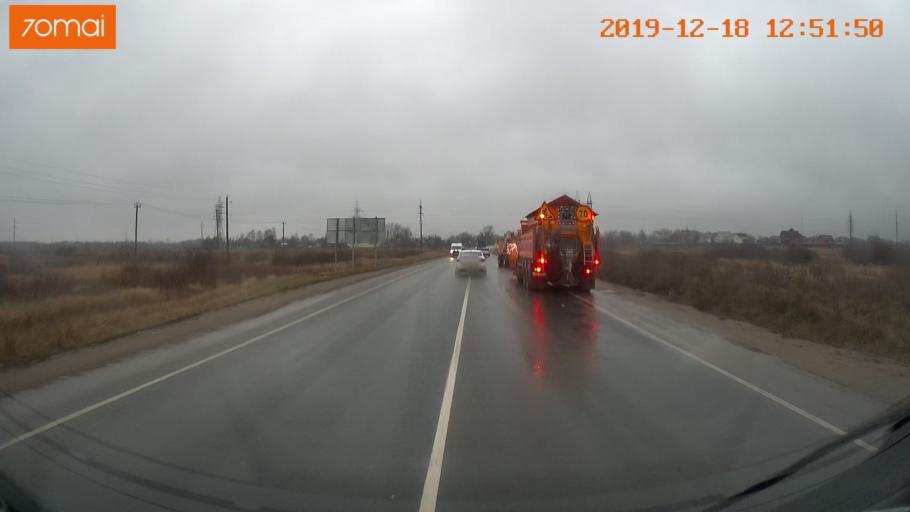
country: RU
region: Moskovskaya
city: Klin
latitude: 56.3069
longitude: 36.6853
